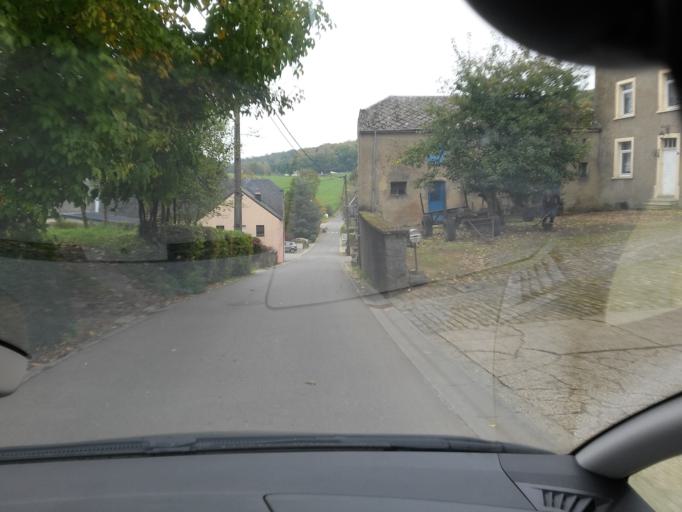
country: BE
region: Wallonia
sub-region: Province du Luxembourg
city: Attert
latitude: 49.7208
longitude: 5.7571
